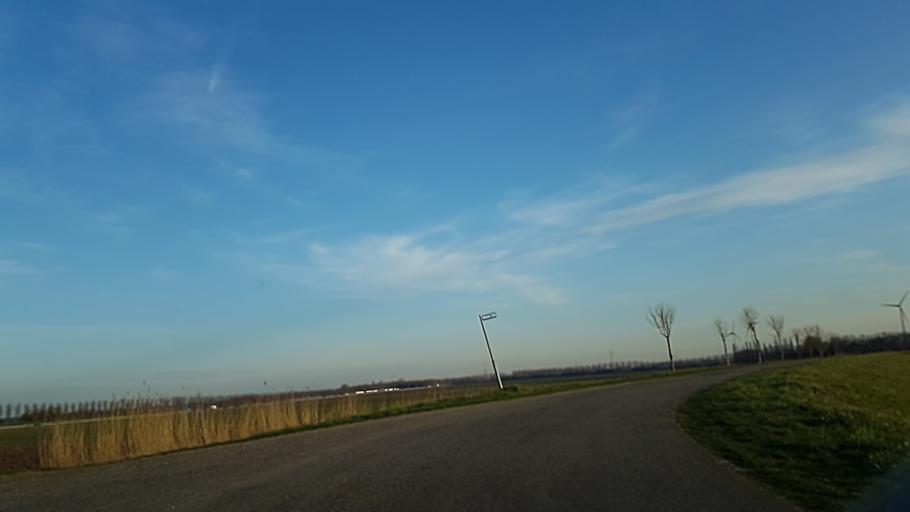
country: NL
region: North Brabant
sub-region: Gemeente Woensdrecht
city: Woensdrecht
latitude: 51.3894
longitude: 4.2901
